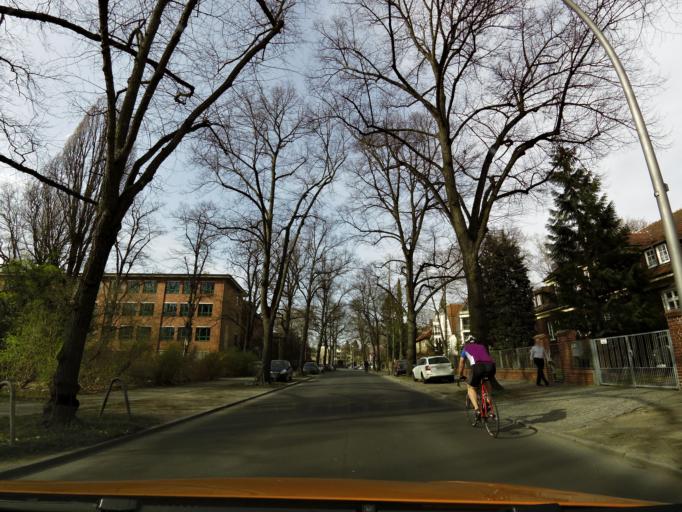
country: DE
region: Berlin
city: Lichterfelde
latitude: 52.4291
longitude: 13.3176
